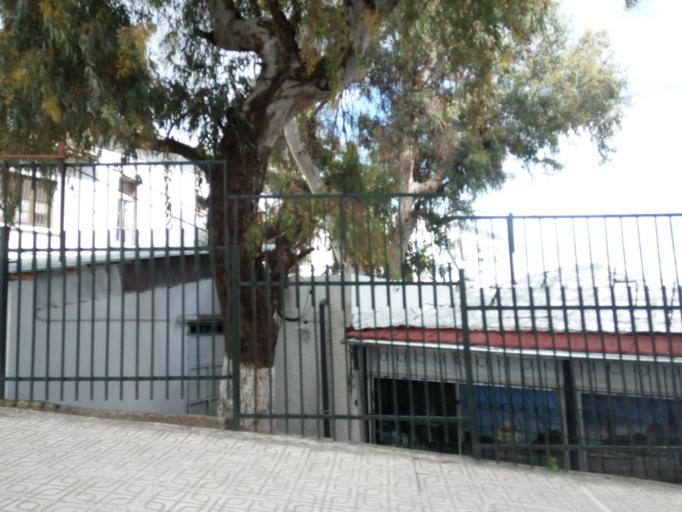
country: DZ
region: Constantine
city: Constantine
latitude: 36.3560
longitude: 6.6097
